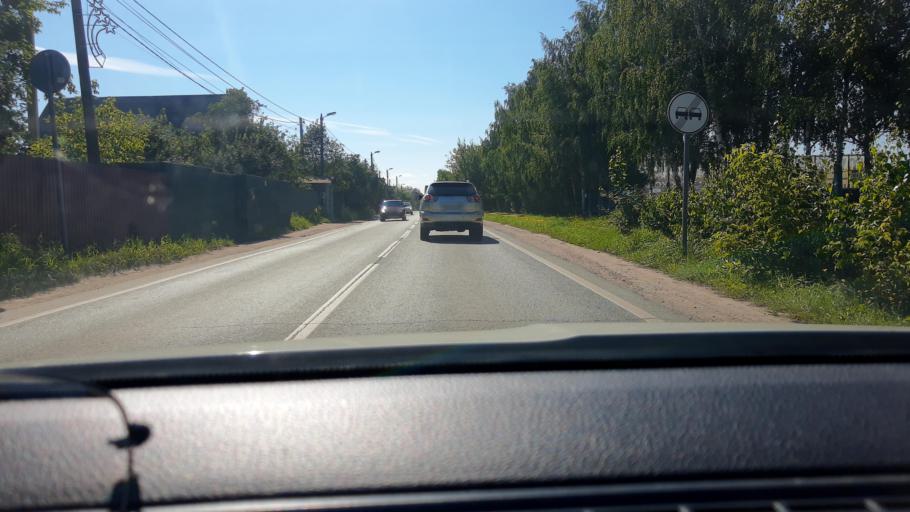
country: RU
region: Moskovskaya
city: Barvikha
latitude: 55.7623
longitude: 37.2285
